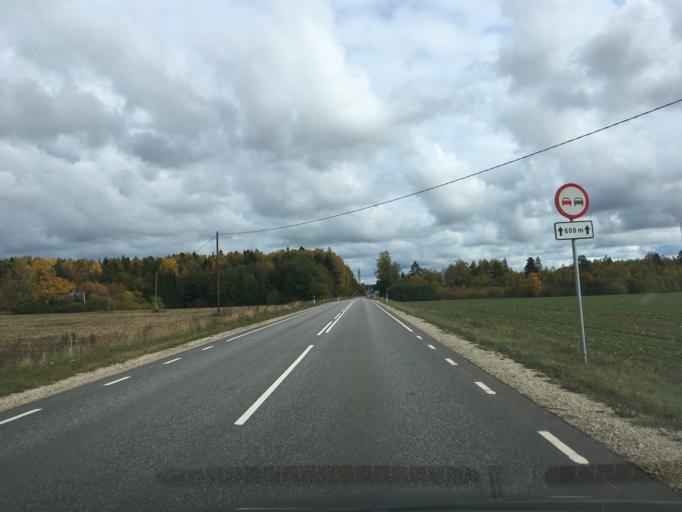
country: EE
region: Harju
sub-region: Anija vald
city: Kehra
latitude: 59.2514
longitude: 25.3162
